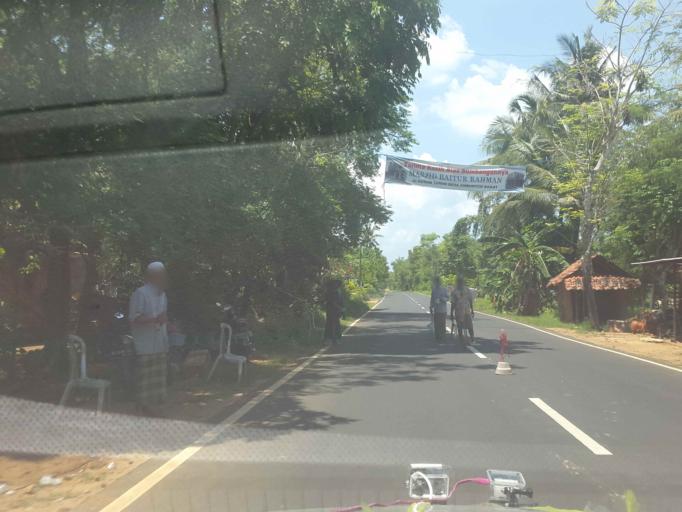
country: ID
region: East Java
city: Durbugan
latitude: -6.8862
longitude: 113.7084
